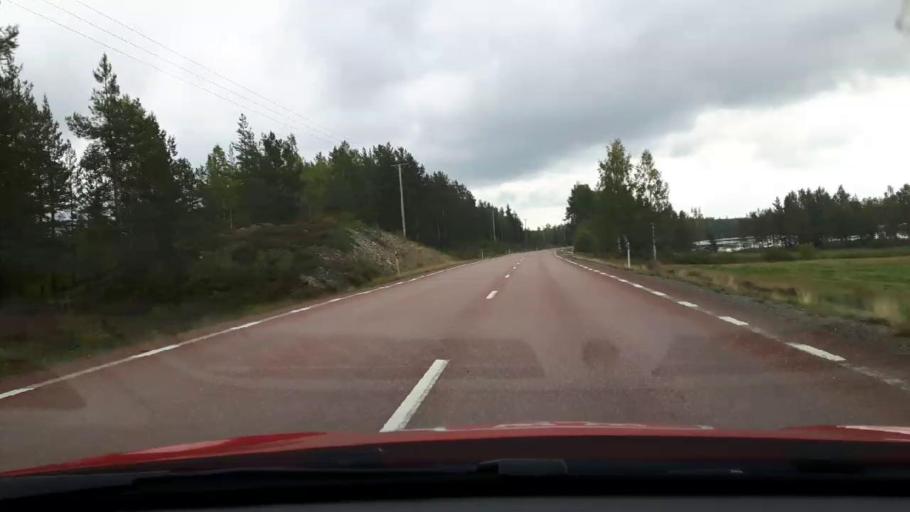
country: SE
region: Gaevleborg
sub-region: Soderhamns Kommun
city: Soderhamn
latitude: 61.1319
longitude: 16.9230
